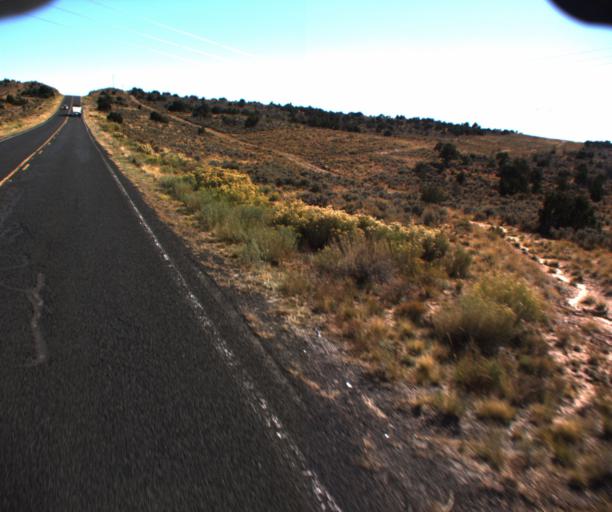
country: US
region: Arizona
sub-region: Apache County
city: Ganado
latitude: 35.6408
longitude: -109.5460
